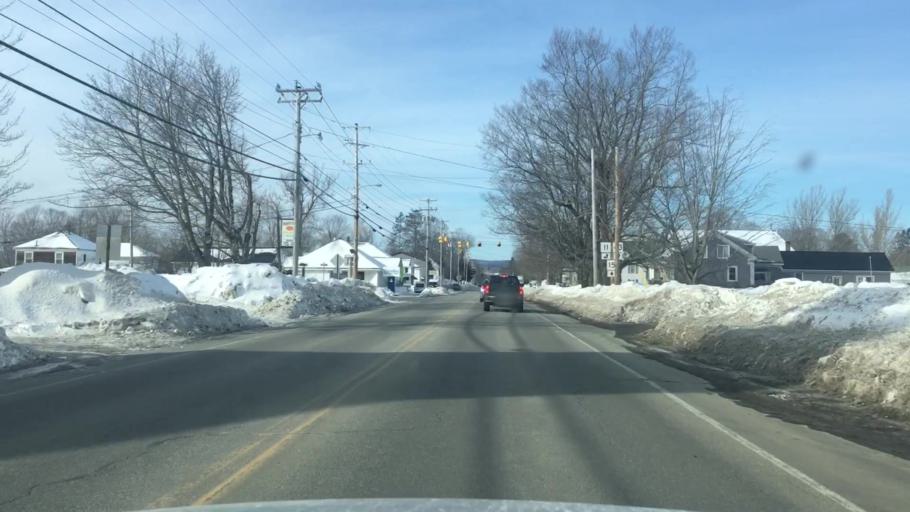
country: US
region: Maine
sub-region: Penobscot County
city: Charleston
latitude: 45.0023
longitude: -69.0228
